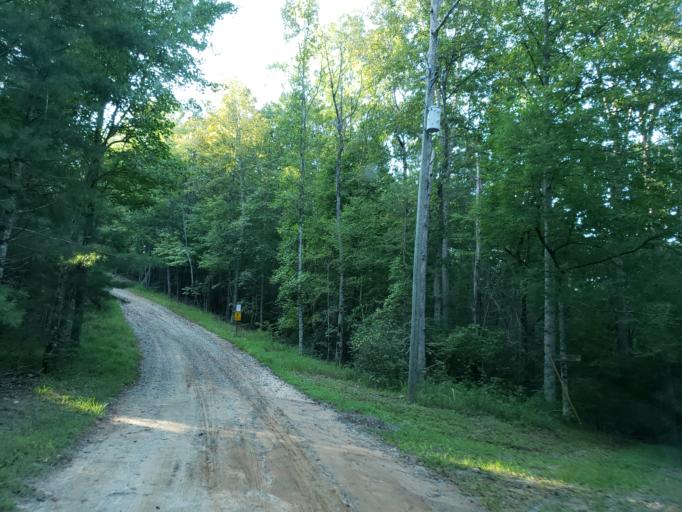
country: US
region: Georgia
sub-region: Fannin County
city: Blue Ridge
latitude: 34.6975
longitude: -84.2653
